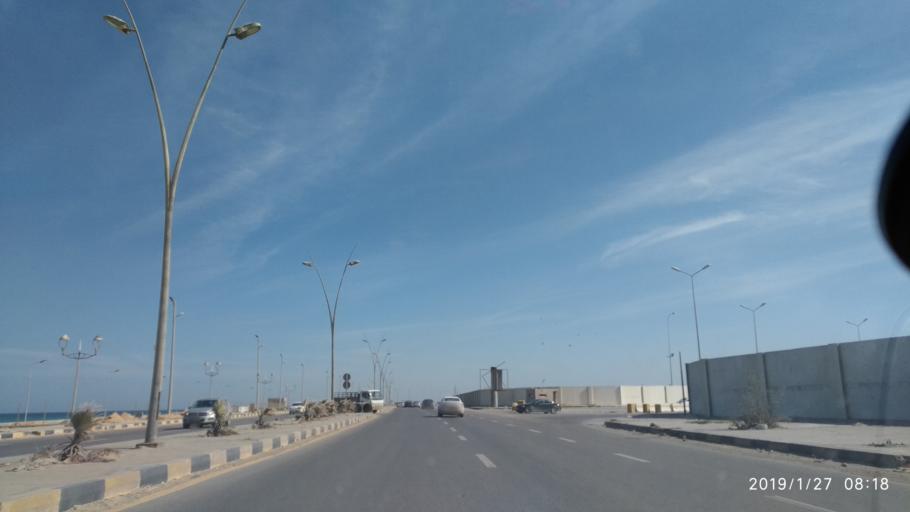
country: LY
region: Tripoli
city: Tagiura
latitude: 32.9084
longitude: 13.2829
